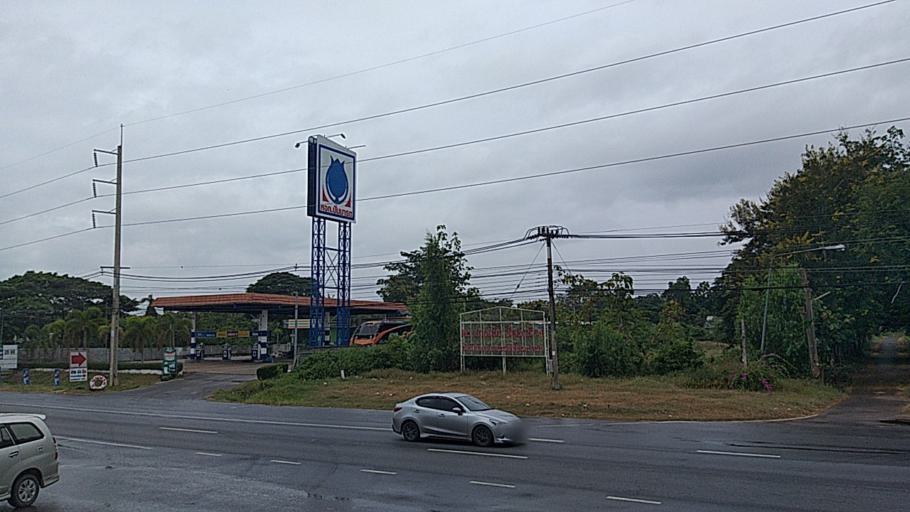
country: TH
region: Maha Sarakham
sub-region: Amphoe Borabue
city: Borabue
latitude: 16.0526
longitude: 103.1306
